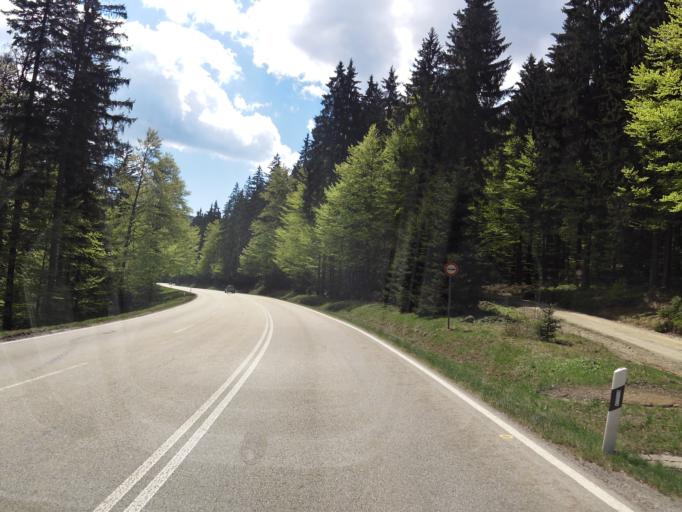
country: DE
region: Bavaria
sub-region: Lower Bavaria
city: Philippsreut
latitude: 48.8520
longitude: 13.6703
